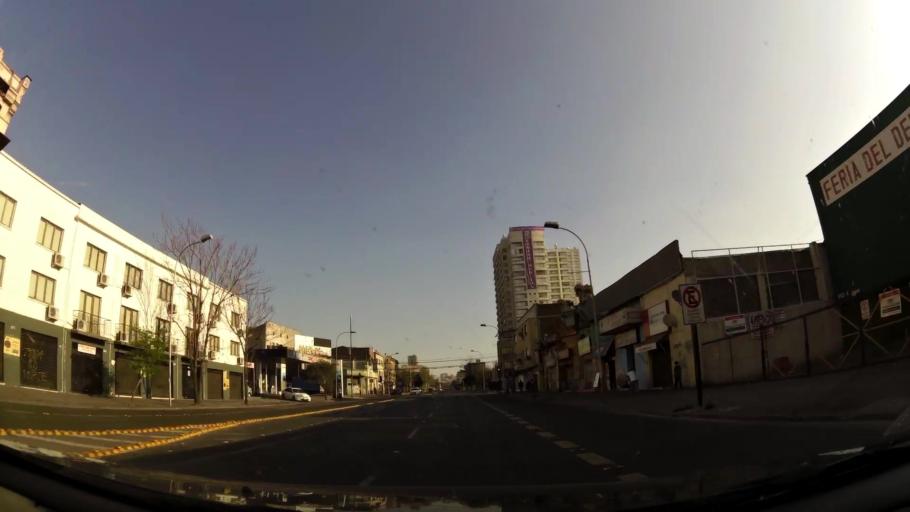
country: CL
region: Santiago Metropolitan
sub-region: Provincia de Santiago
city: Santiago
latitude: -33.4245
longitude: -70.6455
